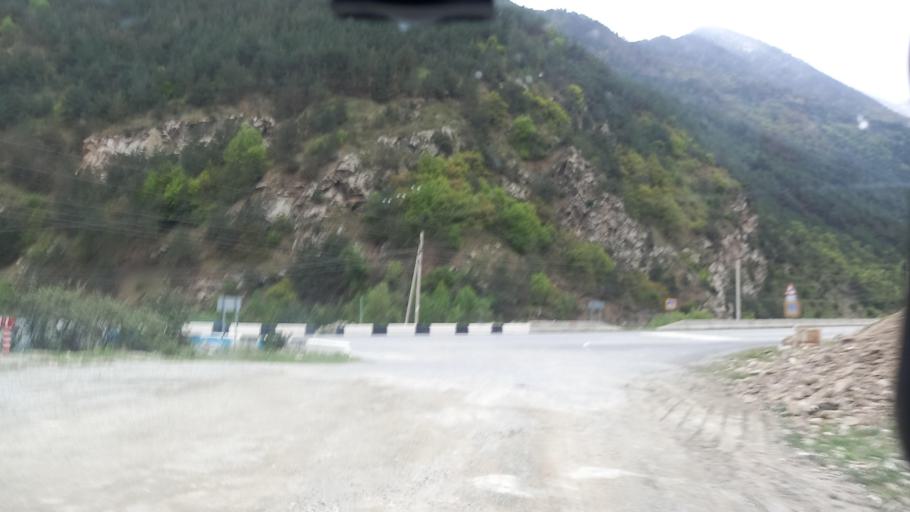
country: RU
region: North Ossetia
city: Mizur
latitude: 42.8393
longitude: 44.0276
